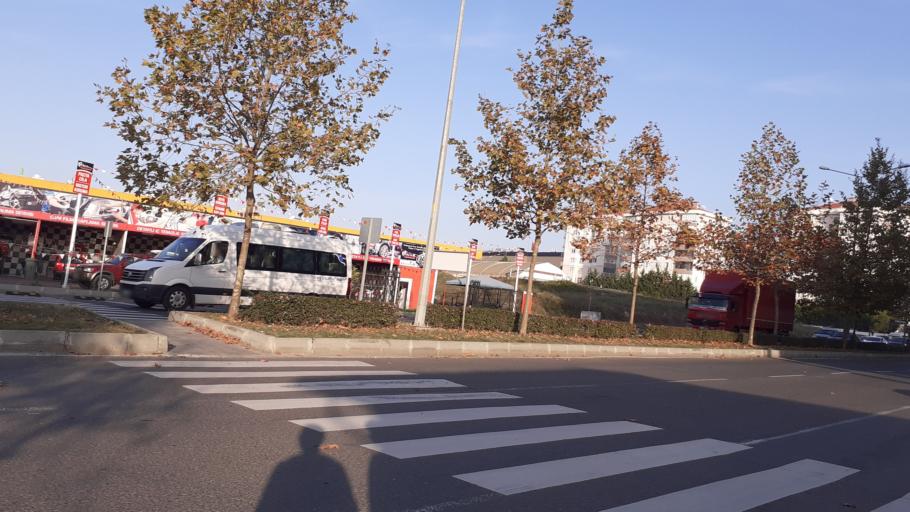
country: TR
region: Tekirdag
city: Corlu
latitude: 41.1489
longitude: 27.8303
